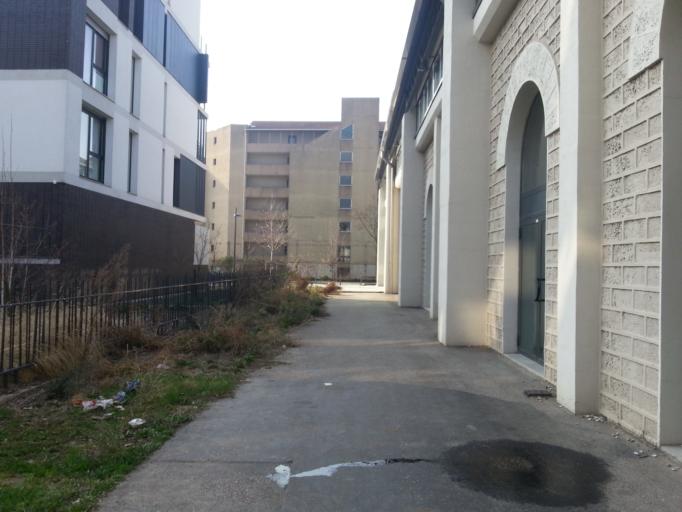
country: FR
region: Rhone-Alpes
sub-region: Departement de l'Isere
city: Seyssinet-Pariset
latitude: 45.1837
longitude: 5.7038
